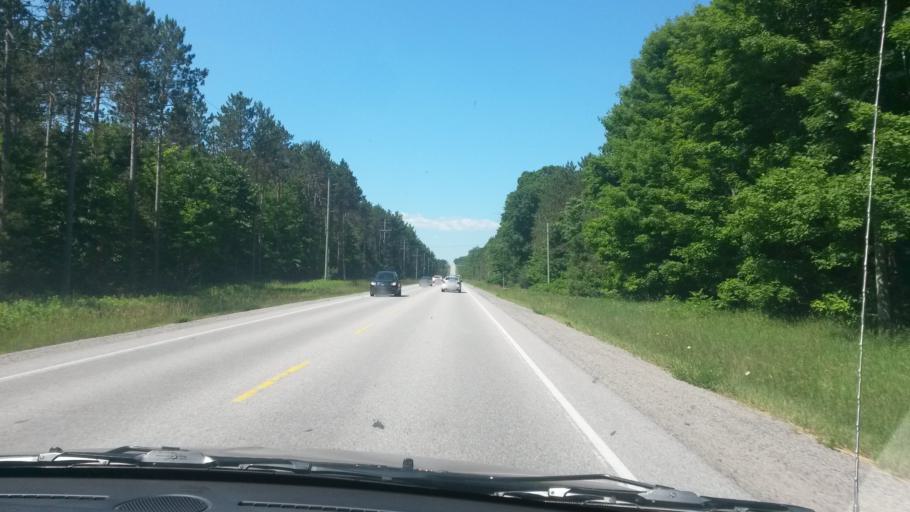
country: CA
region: Ontario
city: Barrie
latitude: 44.5168
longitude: -79.7529
